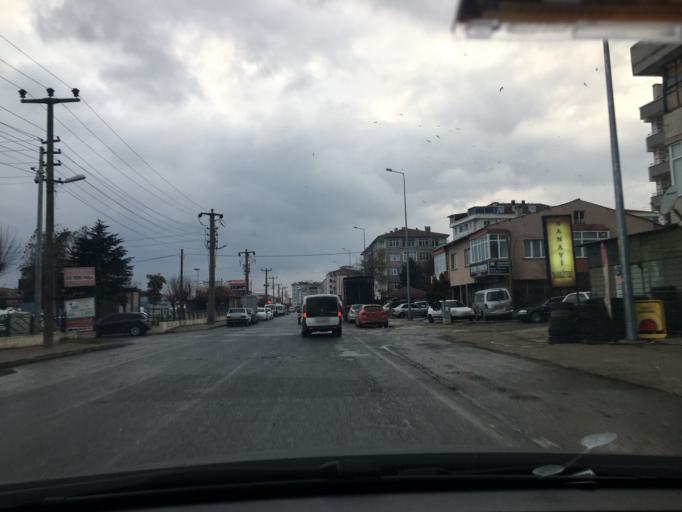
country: TR
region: Tekirdag
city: Cerkezkoey
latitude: 41.2811
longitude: 27.9944
